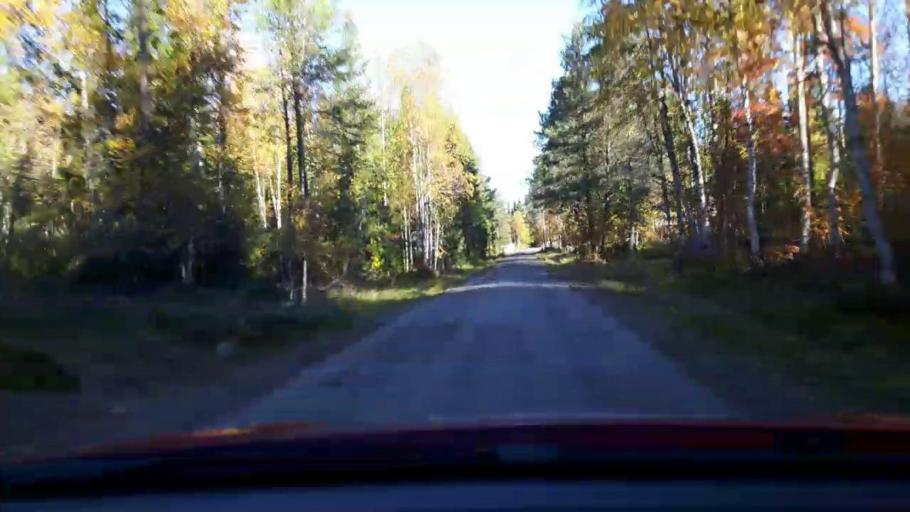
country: SE
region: Jaemtland
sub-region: Stroemsunds Kommun
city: Stroemsund
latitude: 64.3967
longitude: 15.1462
